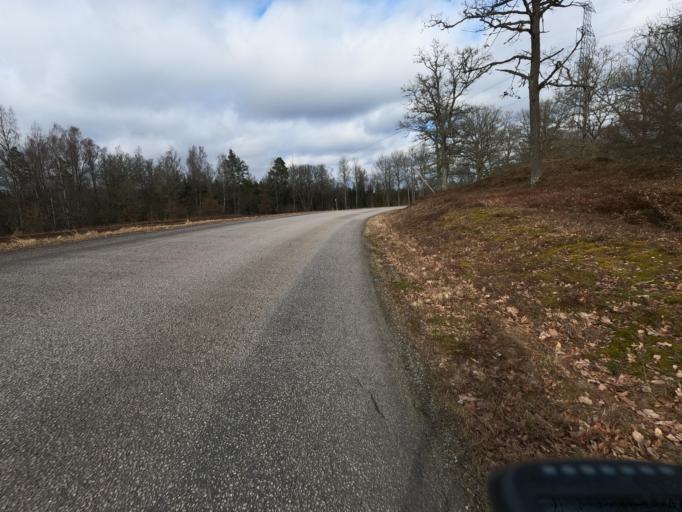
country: SE
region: Kronoberg
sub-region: Alvesta Kommun
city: Alvesta
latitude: 56.8237
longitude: 14.5235
